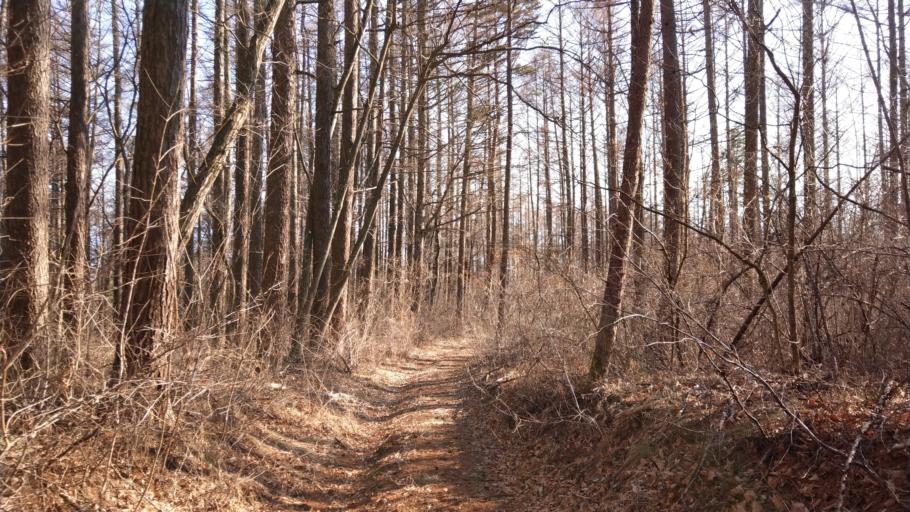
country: JP
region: Nagano
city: Komoro
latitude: 36.3677
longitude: 138.4310
